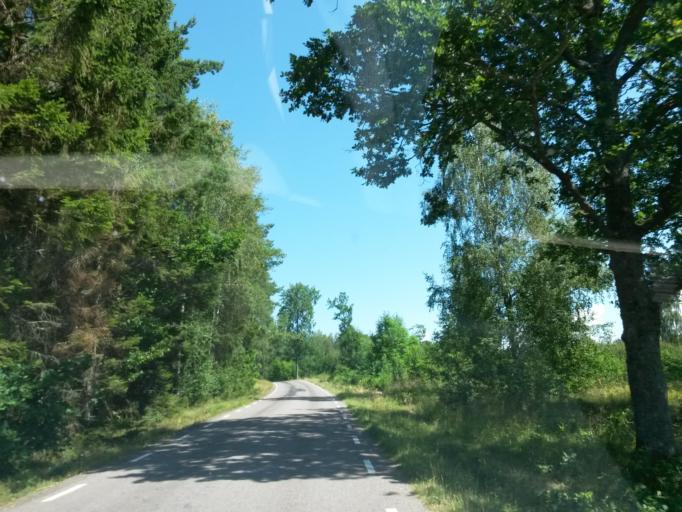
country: SE
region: Vaestra Goetaland
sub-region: Grastorps Kommun
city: Graestorp
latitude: 58.3461
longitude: 12.7729
